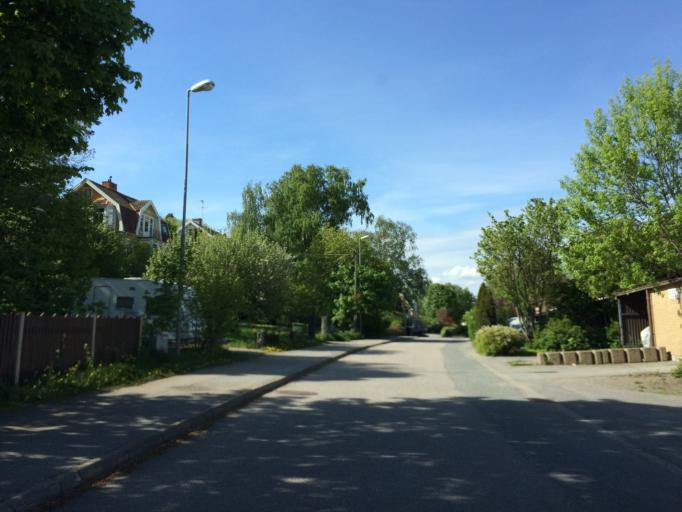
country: SE
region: Stockholm
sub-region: Sollentuna Kommun
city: Sollentuna
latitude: 59.4572
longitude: 17.9220
